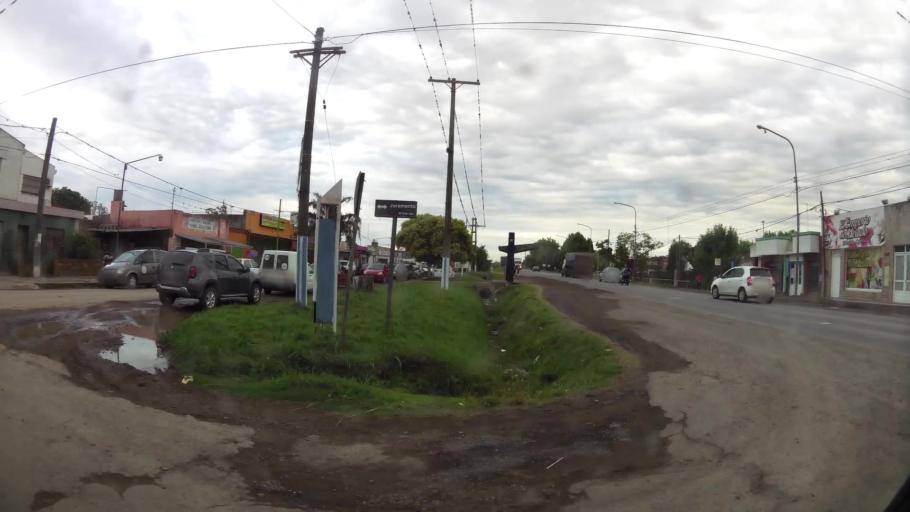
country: AR
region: Buenos Aires
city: San Nicolas de los Arroyos
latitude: -33.3685
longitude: -60.1987
